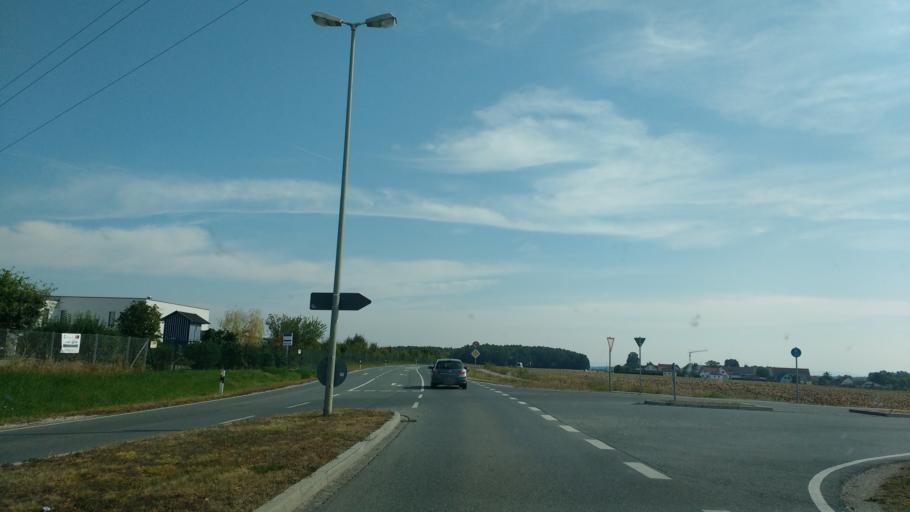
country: DE
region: Bavaria
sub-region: Regierungsbezirk Mittelfranken
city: Weisendorf
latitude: 49.6279
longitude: 10.8408
